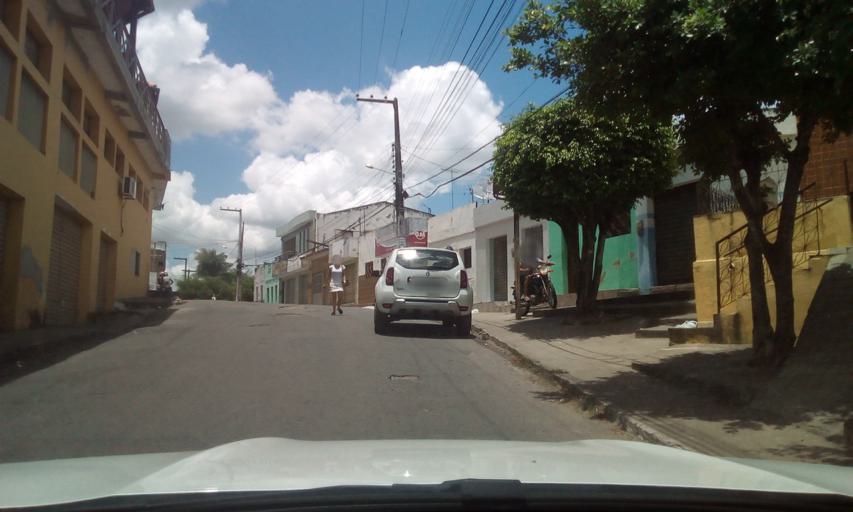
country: BR
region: Paraiba
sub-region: Guarabira
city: Guarabira
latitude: -6.8548
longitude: -35.4852
